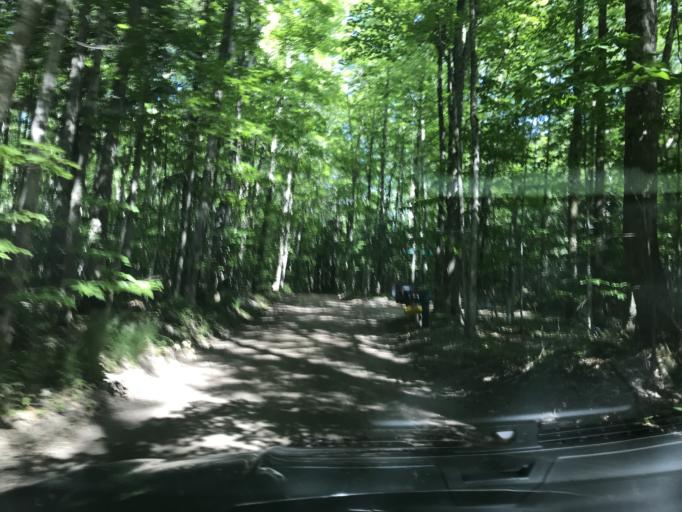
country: US
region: Michigan
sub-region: Cheboygan County
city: Indian River
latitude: 45.5928
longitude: -84.6830
